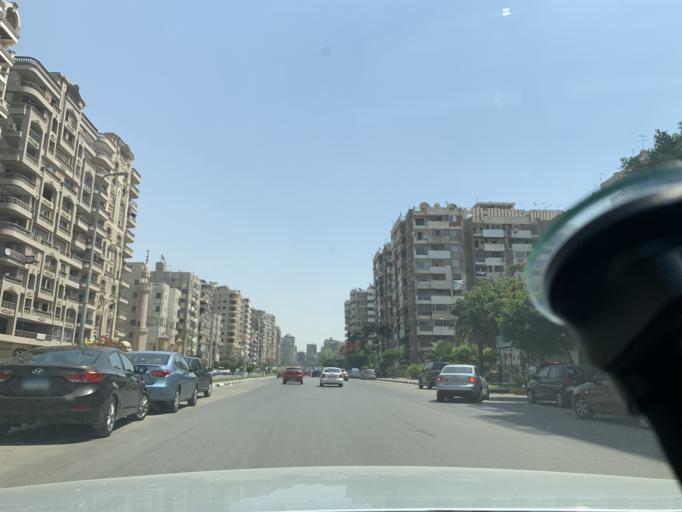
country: EG
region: Muhafazat al Qahirah
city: Cairo
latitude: 30.0677
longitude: 31.3487
